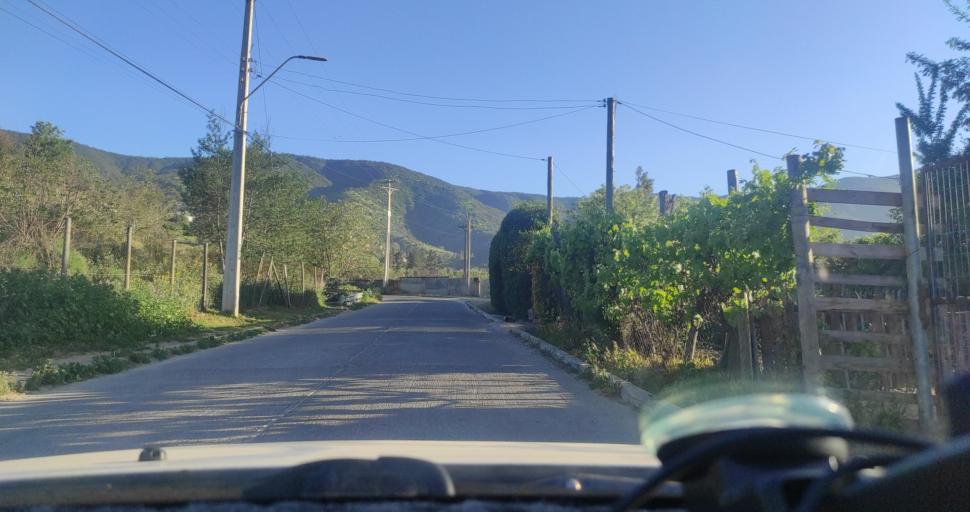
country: CL
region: Valparaiso
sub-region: Provincia de Marga Marga
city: Limache
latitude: -32.9942
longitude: -71.2339
